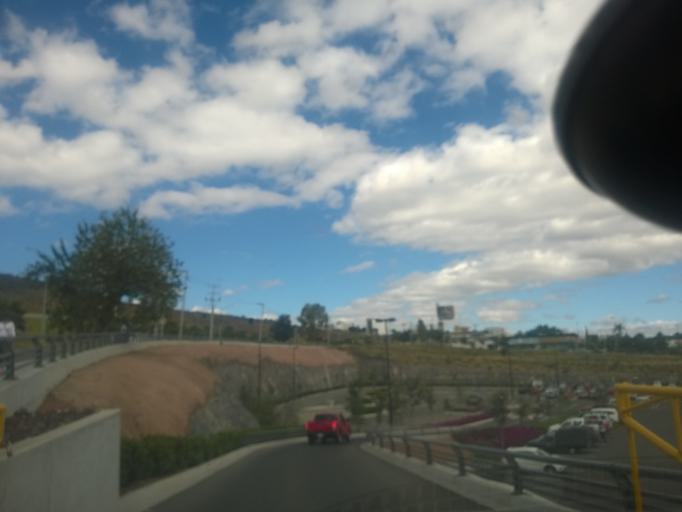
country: MX
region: Guanajuato
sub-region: Leon
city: La Ermita
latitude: 21.1569
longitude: -101.7069
